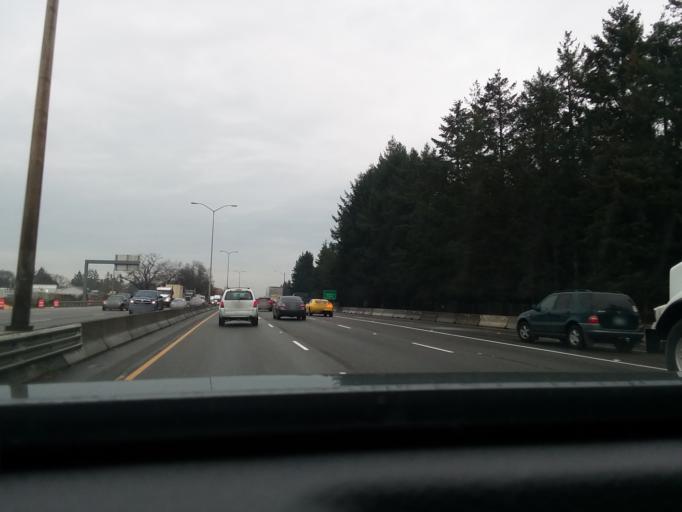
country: US
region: Washington
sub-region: Pierce County
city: Fort Lewis
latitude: 47.1204
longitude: -122.5540
